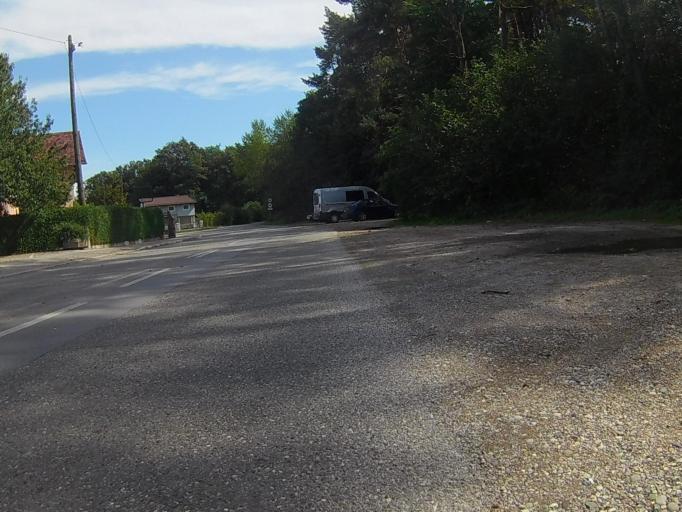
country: SI
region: Miklavz na Dravskem Polju
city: Miklavz na Dravskem Polju
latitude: 46.5264
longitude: 15.6877
